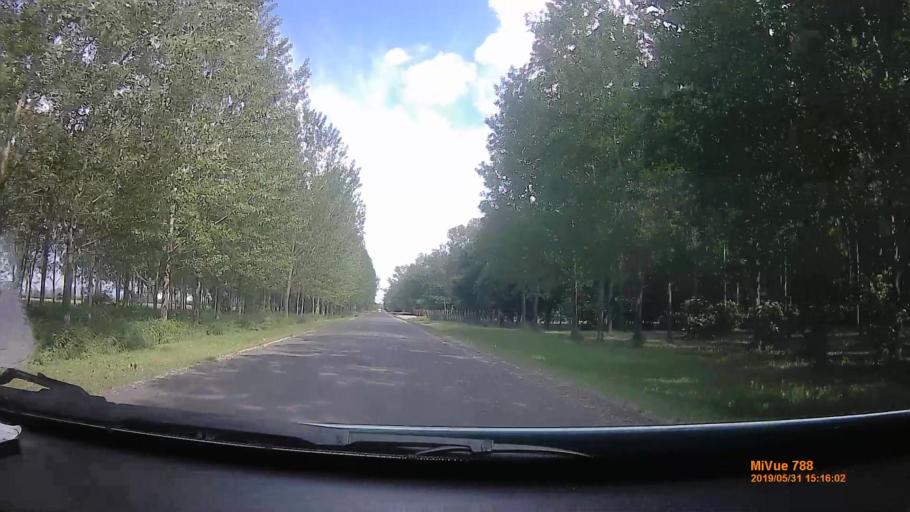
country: HU
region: Borsod-Abauj-Zemplen
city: Taktaharkany
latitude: 48.0896
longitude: 21.0916
